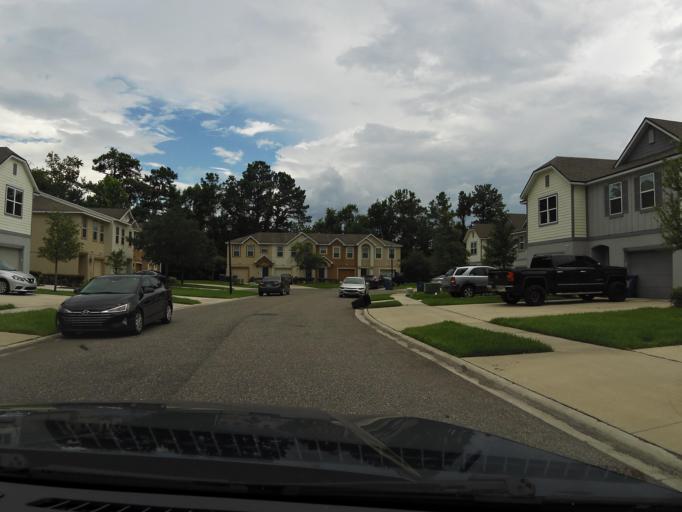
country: US
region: Florida
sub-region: Duval County
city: Jacksonville
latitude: 30.4262
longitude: -81.6977
